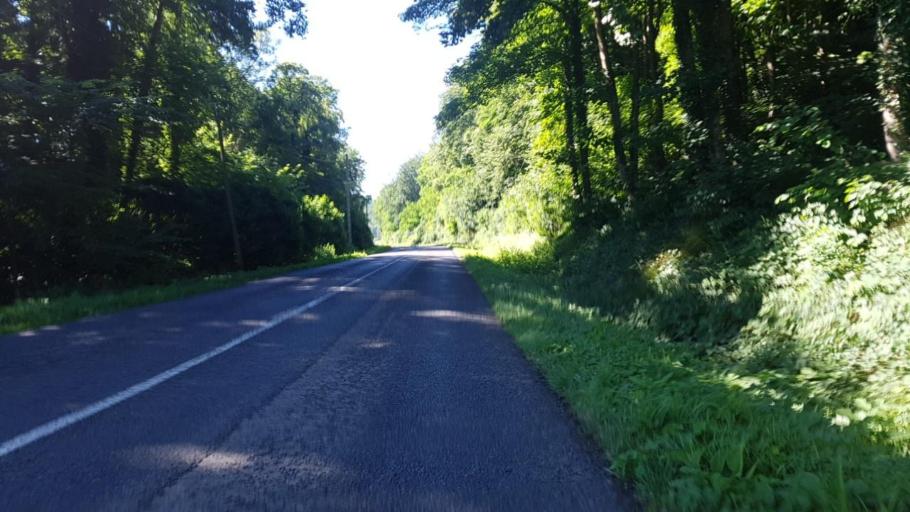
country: FR
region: Picardie
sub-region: Departement de l'Aisne
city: Chezy-sur-Marne
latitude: 48.9915
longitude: 3.3429
